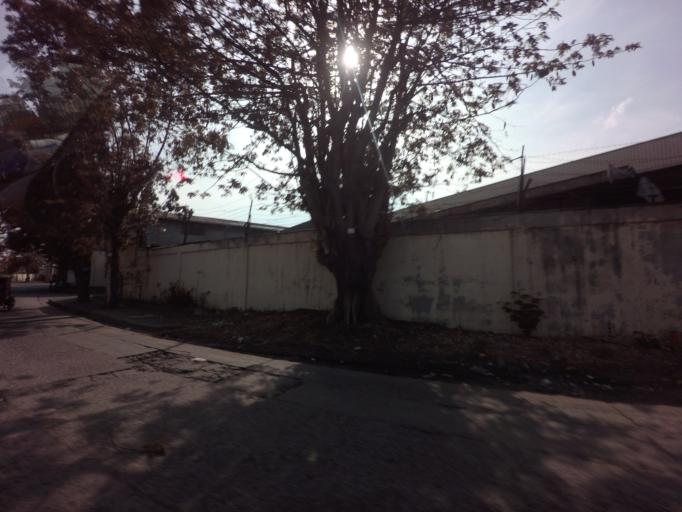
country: PH
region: Calabarzon
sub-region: Province of Rizal
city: Taguig
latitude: 14.5108
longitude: 121.0465
